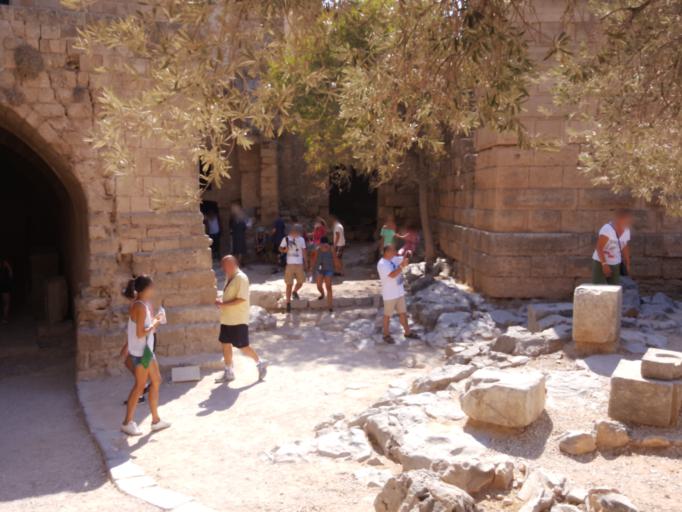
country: GR
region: South Aegean
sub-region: Nomos Dodekanisou
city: Lardos
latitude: 36.0918
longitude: 28.0881
